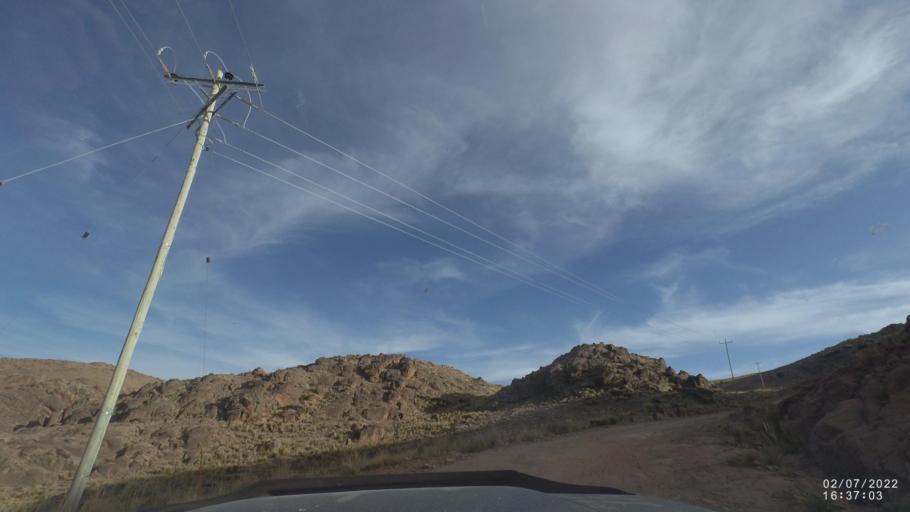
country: BO
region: Cochabamba
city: Irpa Irpa
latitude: -17.9657
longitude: -66.4963
